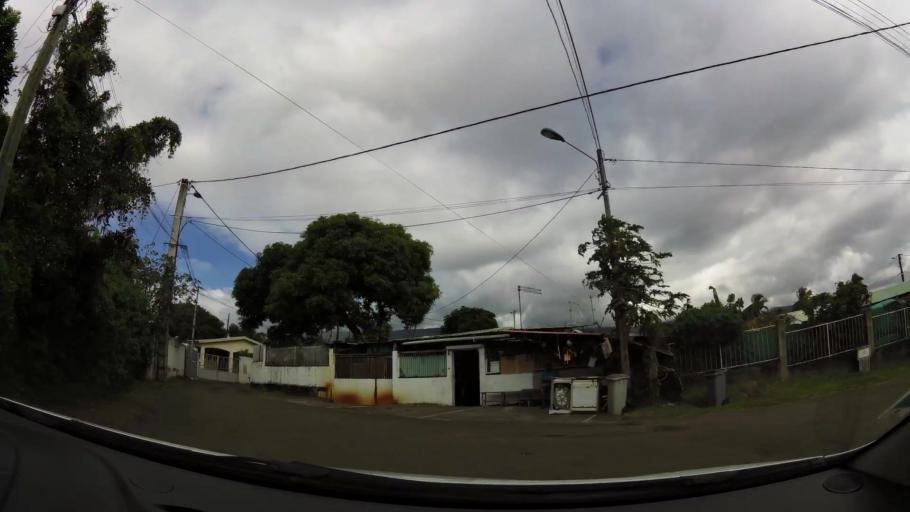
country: RE
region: Reunion
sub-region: Reunion
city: Sainte-Marie
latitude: -20.8979
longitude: 55.5275
